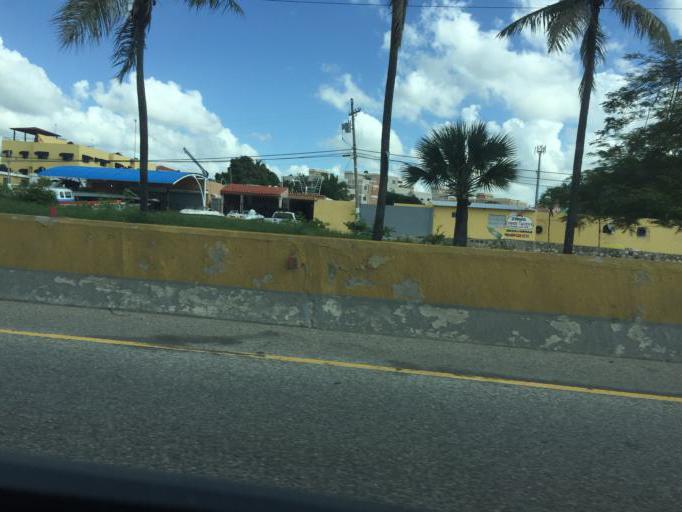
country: DO
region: Santo Domingo
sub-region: Santo Domingo
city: Santo Domingo Este
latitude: 18.4788
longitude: -69.8372
